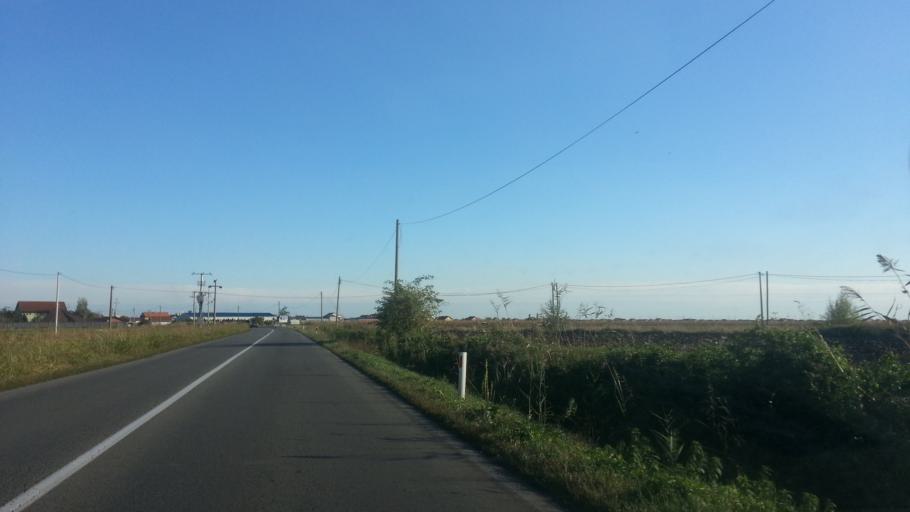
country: RS
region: Autonomna Pokrajina Vojvodina
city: Nova Pazova
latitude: 44.9177
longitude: 20.2535
